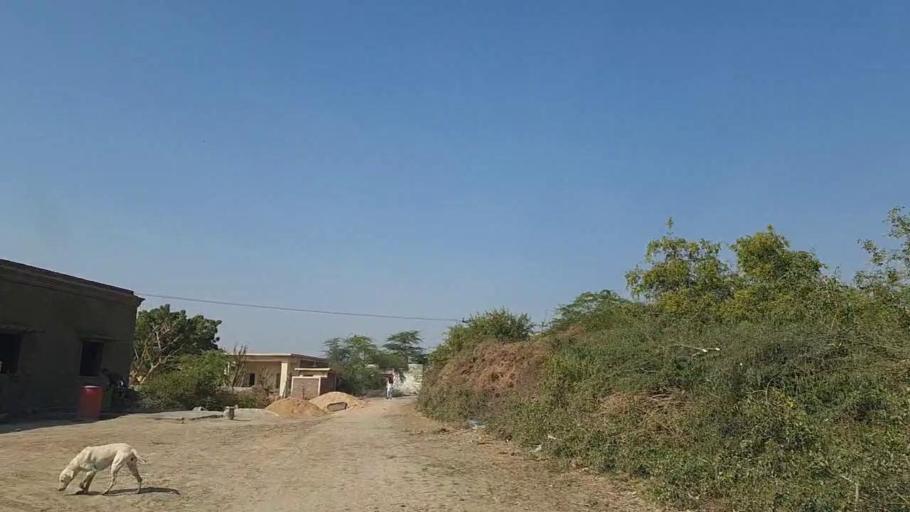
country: PK
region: Sindh
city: Naukot
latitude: 24.8966
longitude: 69.4494
